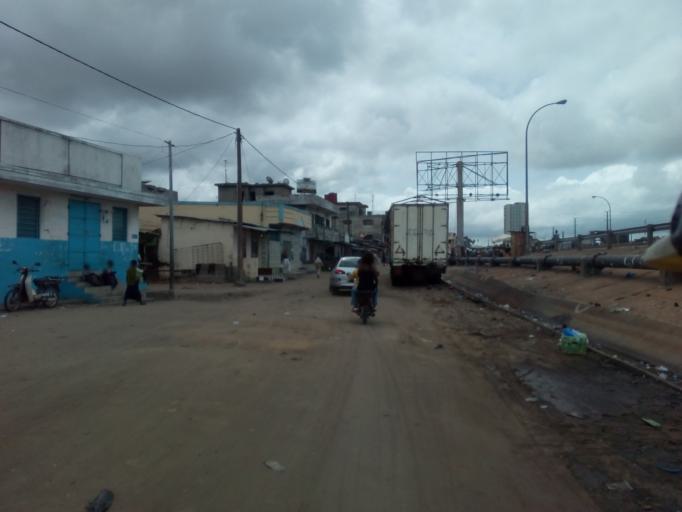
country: BJ
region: Littoral
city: Cotonou
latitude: 6.3719
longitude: 2.4406
